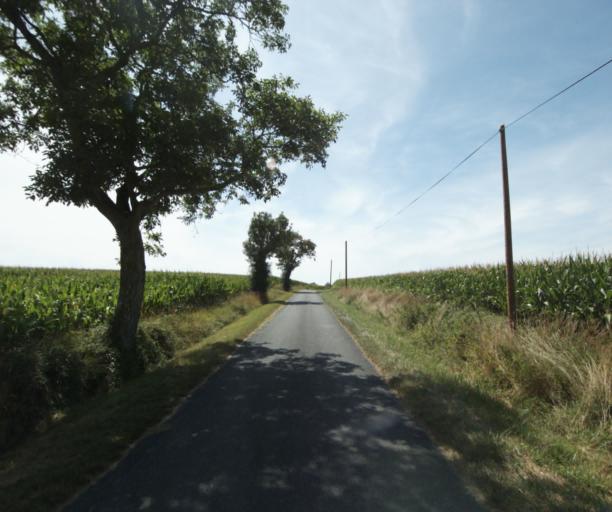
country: FR
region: Midi-Pyrenees
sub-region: Departement du Tarn
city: Puylaurens
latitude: 43.5256
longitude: 2.0169
